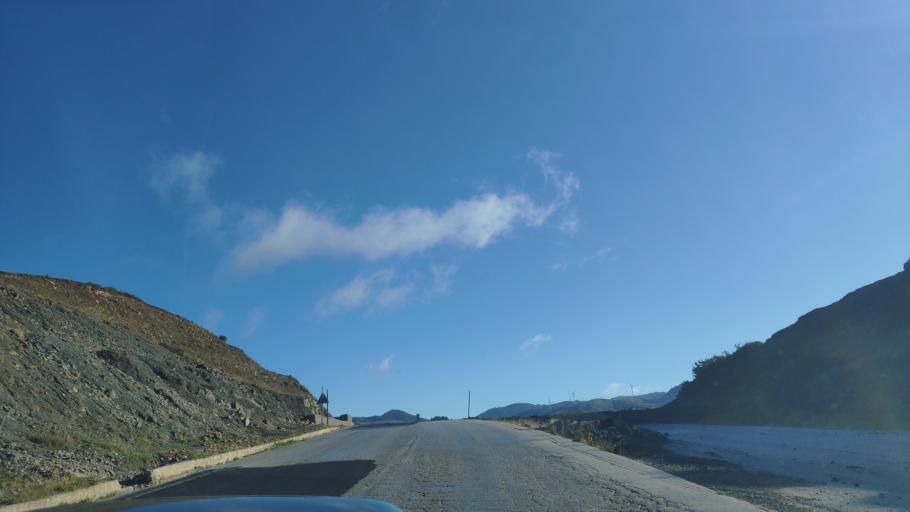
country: GR
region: Epirus
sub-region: Nomos Ioanninon
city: Metsovo
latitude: 39.7900
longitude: 21.1639
